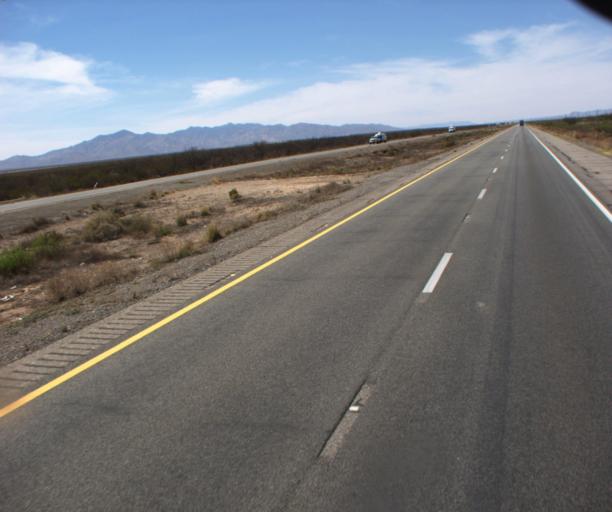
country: US
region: Arizona
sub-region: Cochise County
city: Willcox
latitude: 32.2795
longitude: -109.2753
